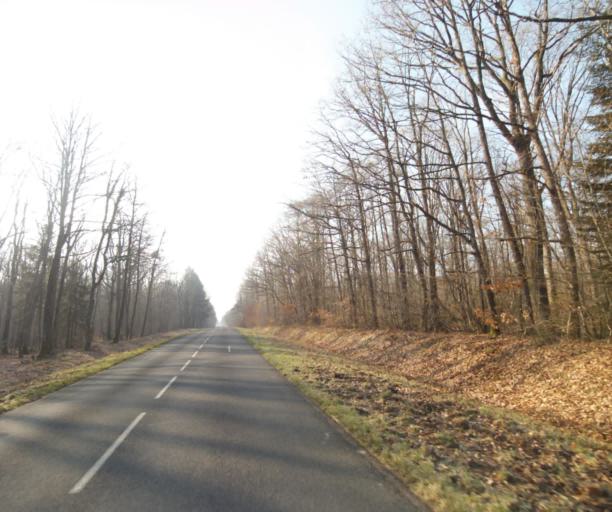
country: FR
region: Champagne-Ardenne
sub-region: Departement de la Haute-Marne
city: Laneuville-a-Remy
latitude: 48.4706
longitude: 4.9199
